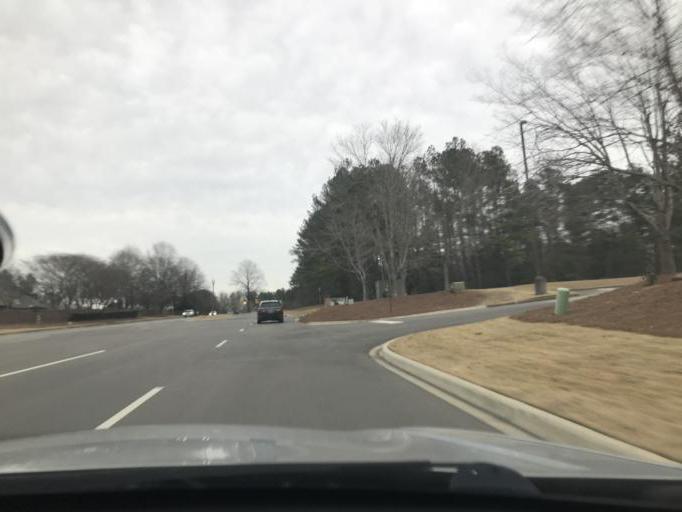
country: US
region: Alabama
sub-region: Jefferson County
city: Cahaba Heights
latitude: 33.4746
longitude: -86.6927
